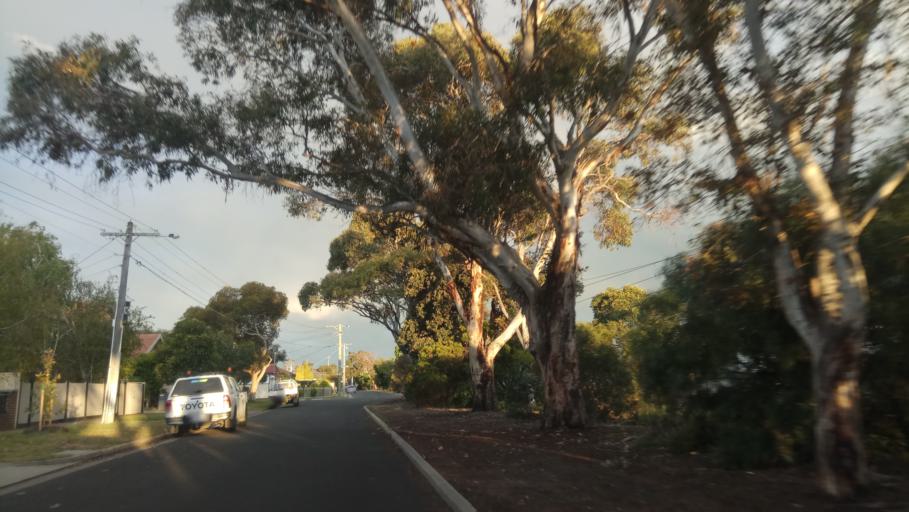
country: AU
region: Victoria
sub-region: Hobsons Bay
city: Altona
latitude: -37.8676
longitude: 144.8349
